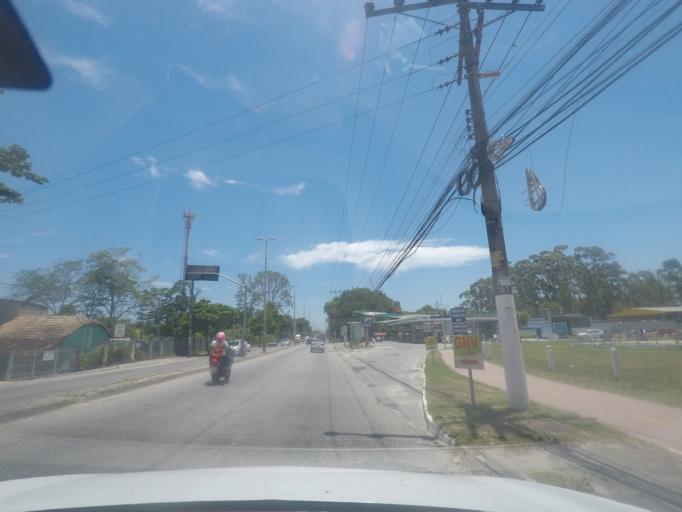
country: BR
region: Rio de Janeiro
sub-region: Itaguai
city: Itaguai
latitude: -22.9040
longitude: -43.6829
